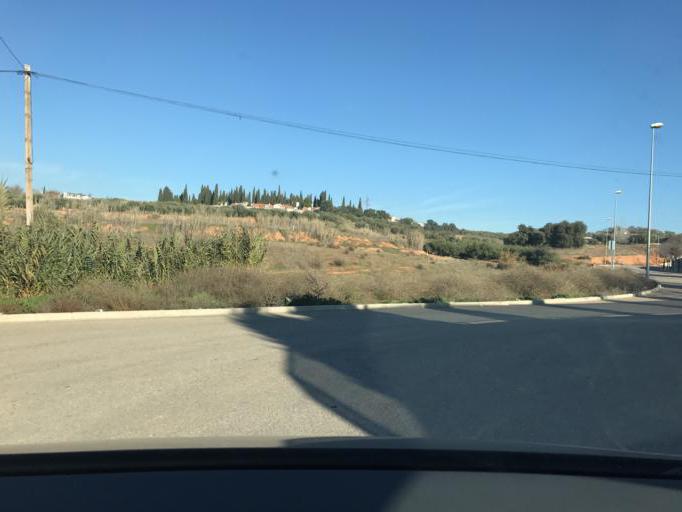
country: ES
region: Andalusia
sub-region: Provincia de Granada
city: Peligros
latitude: 37.2352
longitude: -3.6218
